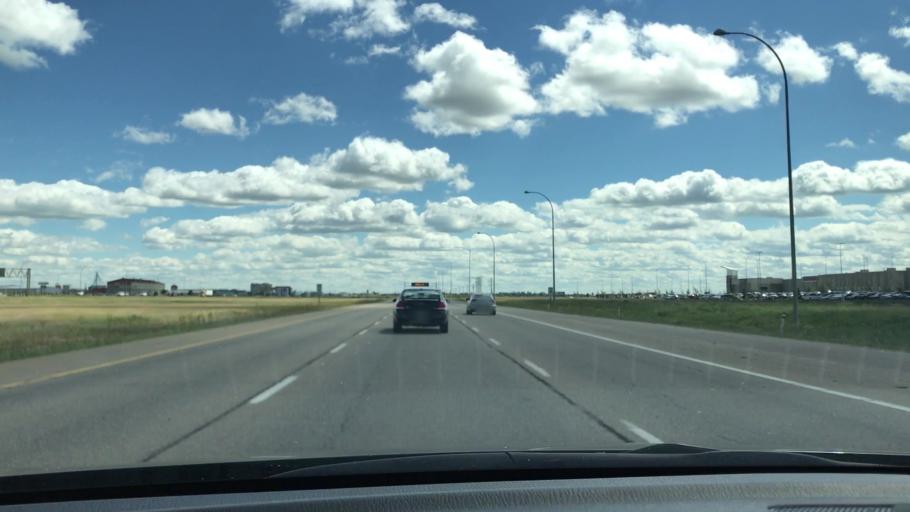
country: CA
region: Alberta
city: Leduc
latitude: 53.3047
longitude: -113.5498
